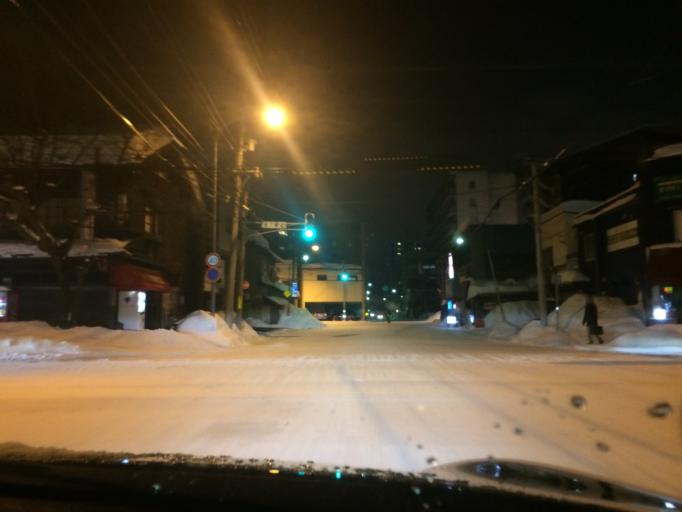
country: JP
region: Hokkaido
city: Sapporo
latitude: 43.0715
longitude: 141.3595
